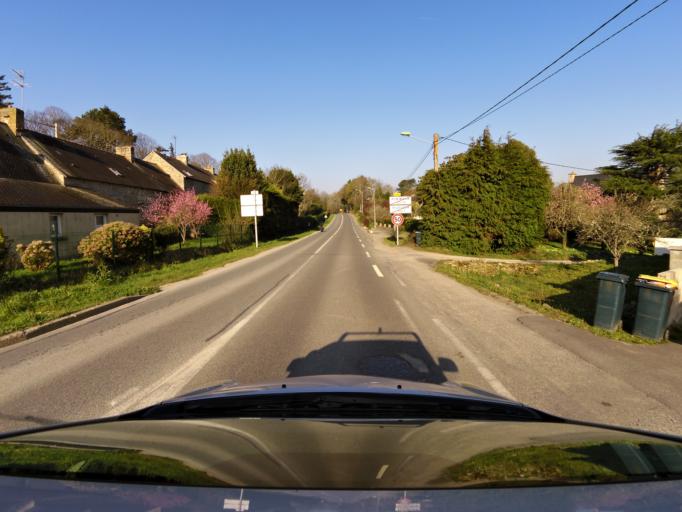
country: FR
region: Brittany
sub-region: Departement du Morbihan
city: Ploemeur
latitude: 47.7384
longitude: -3.4447
